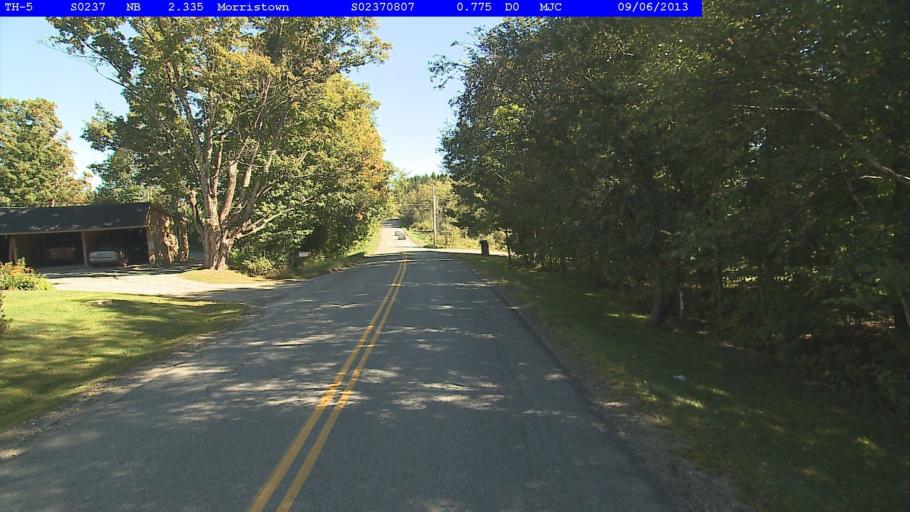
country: US
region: Vermont
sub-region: Lamoille County
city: Morristown
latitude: 44.5115
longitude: -72.6463
